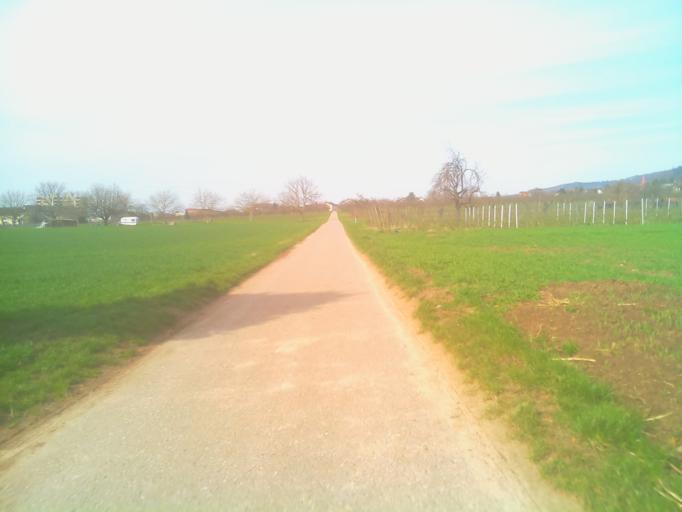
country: DE
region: Baden-Wuerttemberg
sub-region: Karlsruhe Region
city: Schriesheim
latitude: 49.4903
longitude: 8.6592
